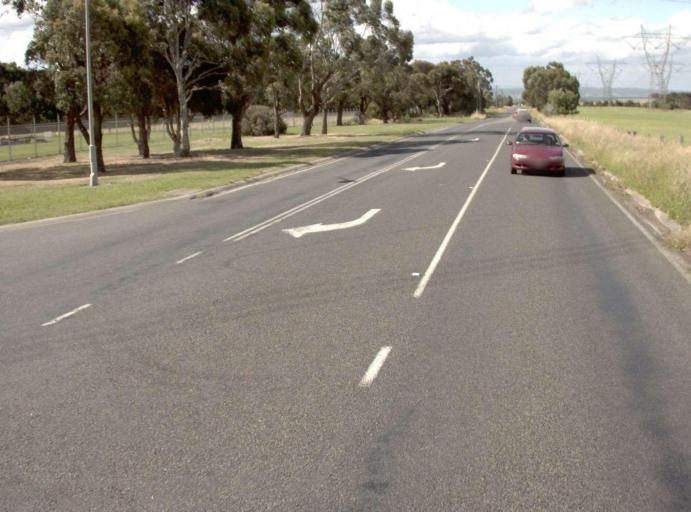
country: AU
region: Victoria
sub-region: Latrobe
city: Morwell
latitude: -38.2801
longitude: 146.4317
